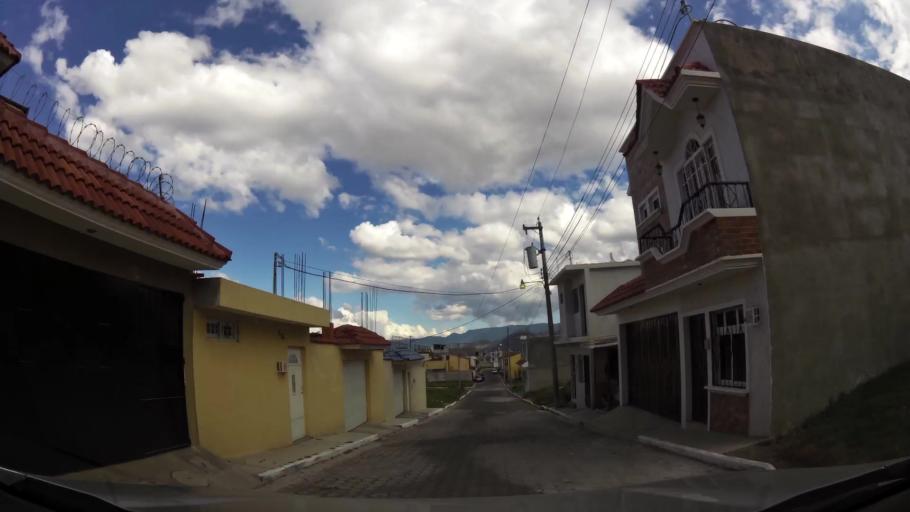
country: GT
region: Quetzaltenango
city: Quetzaltenango
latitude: 14.8359
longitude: -91.5513
